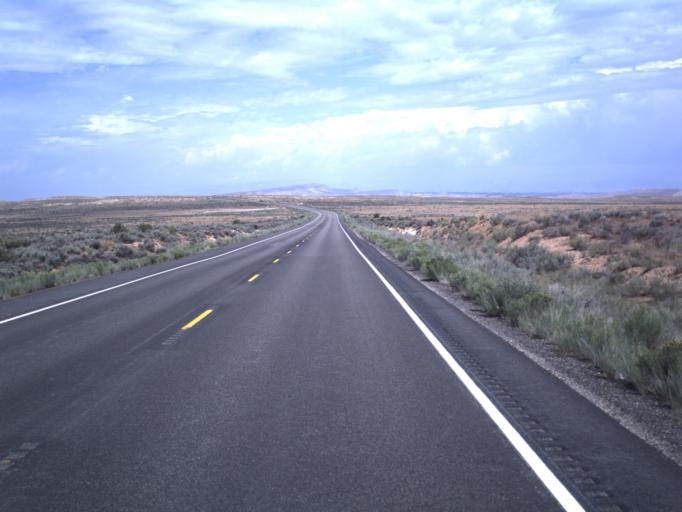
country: US
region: Utah
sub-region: Uintah County
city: Naples
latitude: 40.2438
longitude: -109.4185
